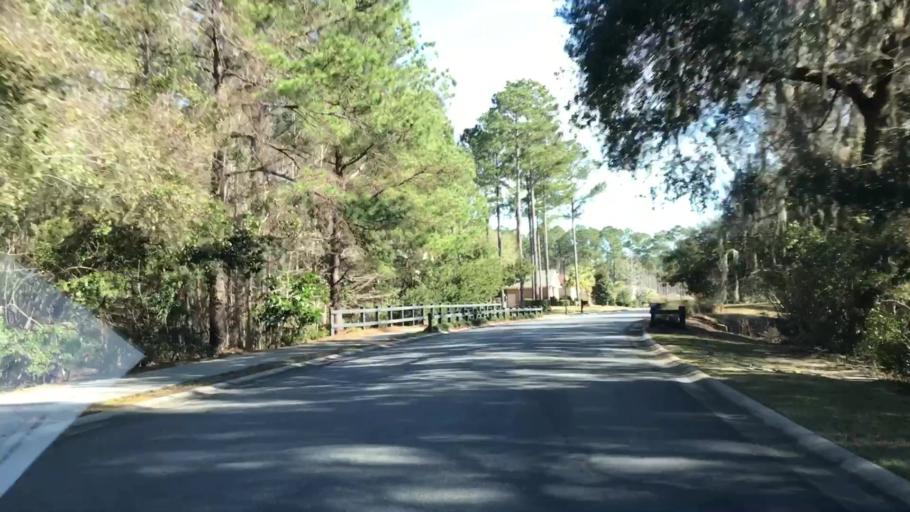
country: US
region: South Carolina
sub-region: Beaufort County
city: Bluffton
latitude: 32.2528
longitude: -80.9207
